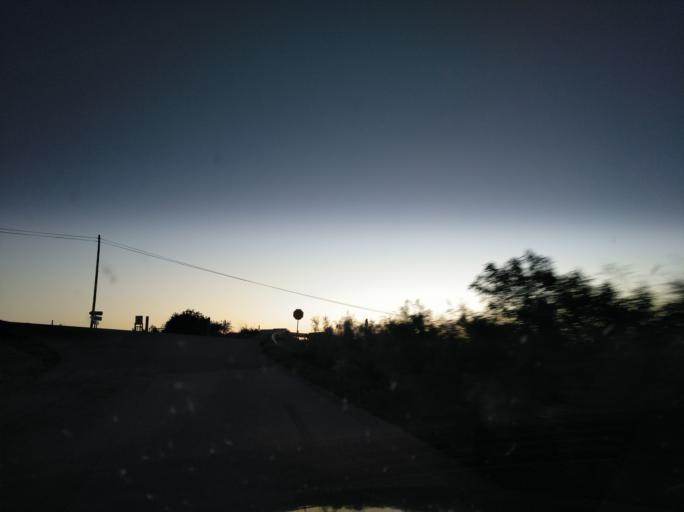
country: PT
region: Faro
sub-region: Vila Real de Santo Antonio
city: Monte Gordo
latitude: 37.1953
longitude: -7.5156
